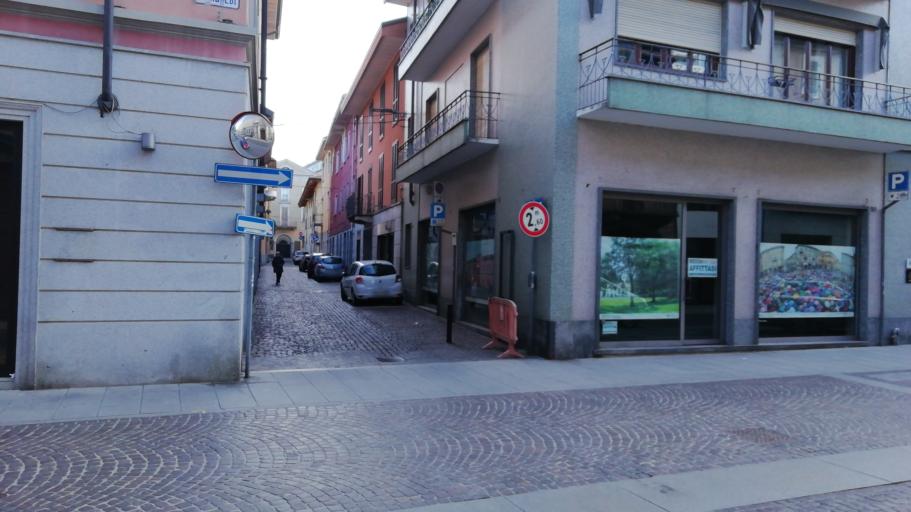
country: IT
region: Piedmont
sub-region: Provincia di Novara
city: Borgomanero
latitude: 45.6999
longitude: 8.4614
